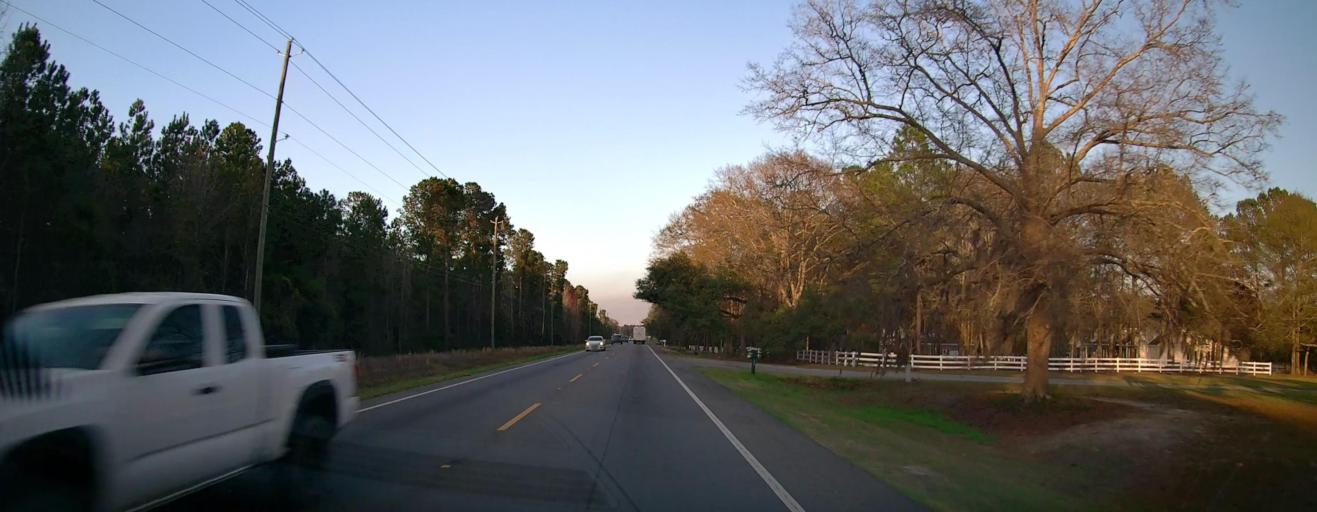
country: US
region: Georgia
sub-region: Effingham County
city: Guyton
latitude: 32.1914
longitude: -81.4450
